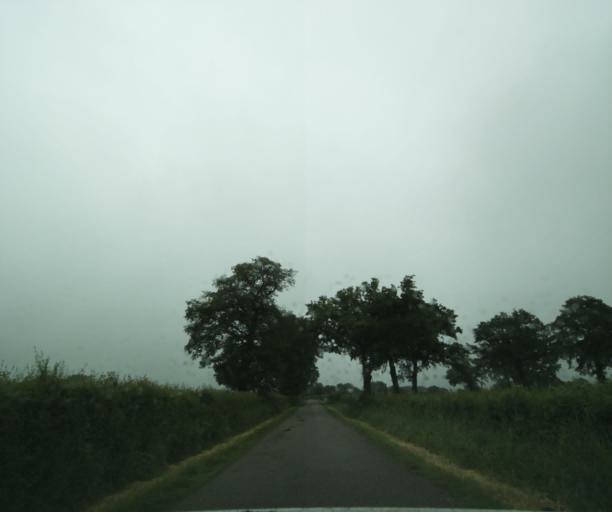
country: FR
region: Bourgogne
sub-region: Departement de Saone-et-Loire
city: Charolles
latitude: 46.4218
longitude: 4.3175
